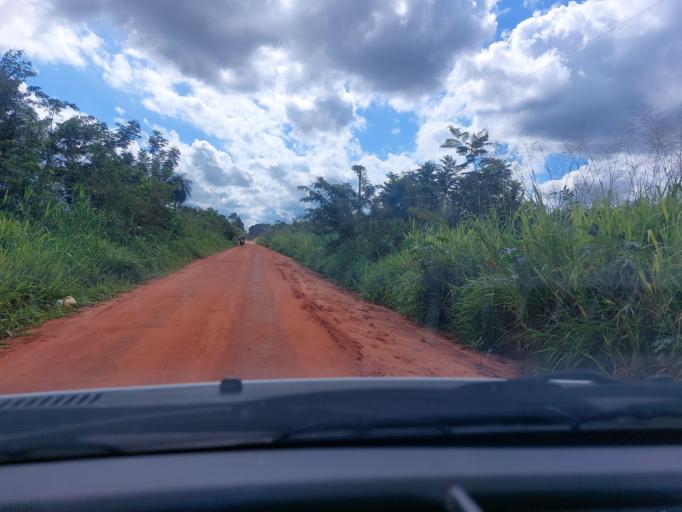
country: PY
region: San Pedro
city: Itacurubi del Rosario
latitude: -24.5340
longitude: -56.5656
